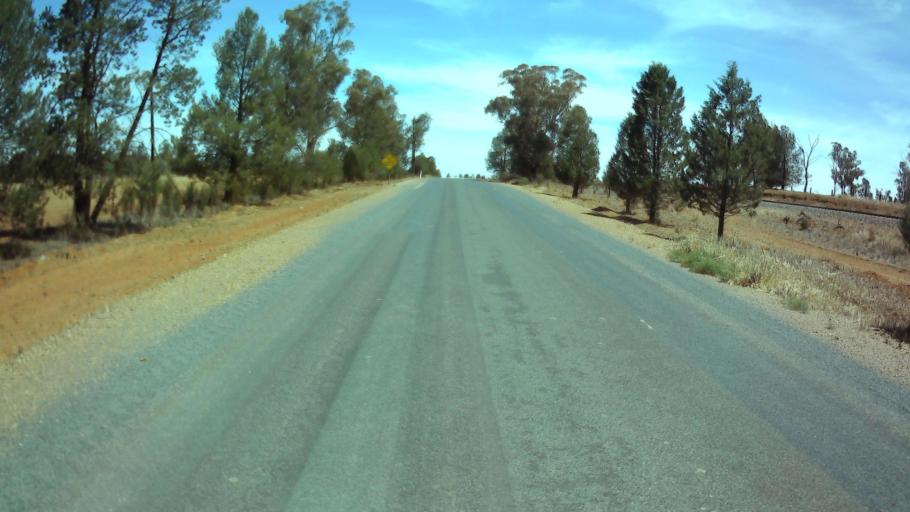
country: AU
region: New South Wales
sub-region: Weddin
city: Grenfell
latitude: -33.7711
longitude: 147.7568
